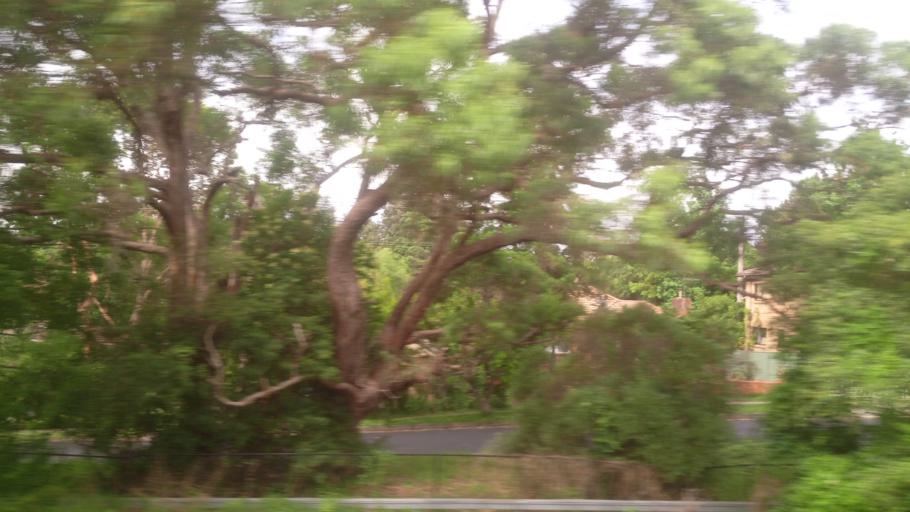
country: AU
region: New South Wales
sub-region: Blue Mountains Municipality
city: Blaxland
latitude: -33.6967
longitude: 150.5499
